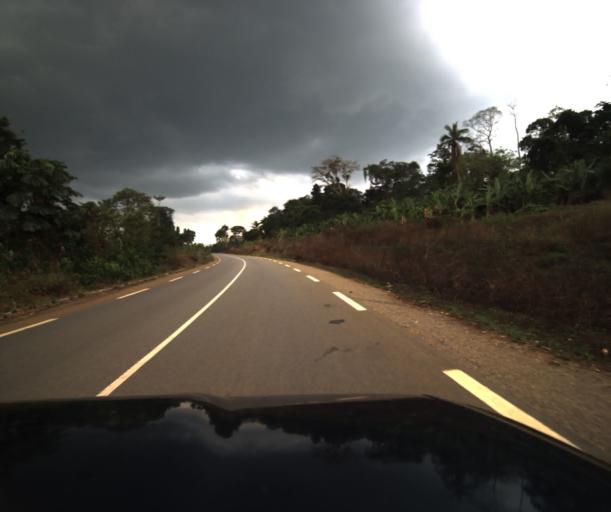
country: CM
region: Centre
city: Mbankomo
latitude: 3.6724
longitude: 11.3495
